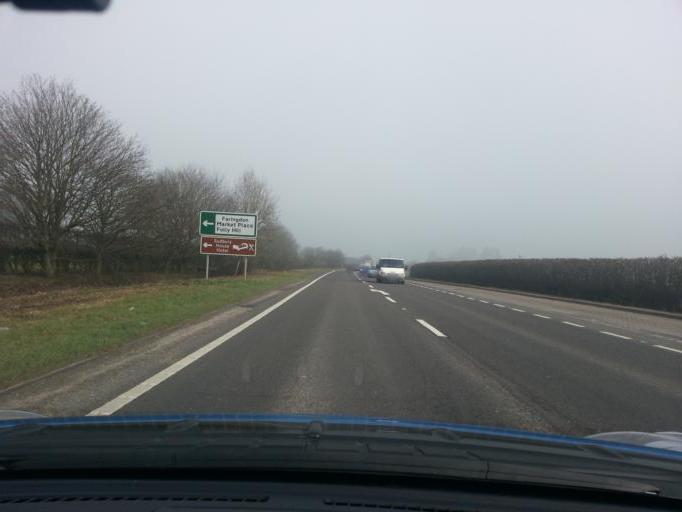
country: GB
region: England
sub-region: Oxfordshire
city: Faringdon
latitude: 51.6603
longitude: -1.5643
